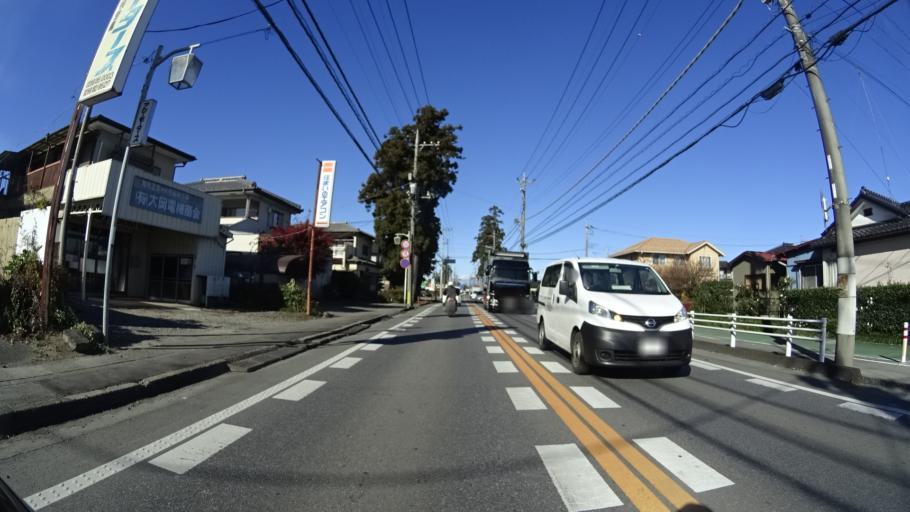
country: JP
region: Tochigi
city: Kanuma
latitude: 36.5357
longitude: 139.7472
